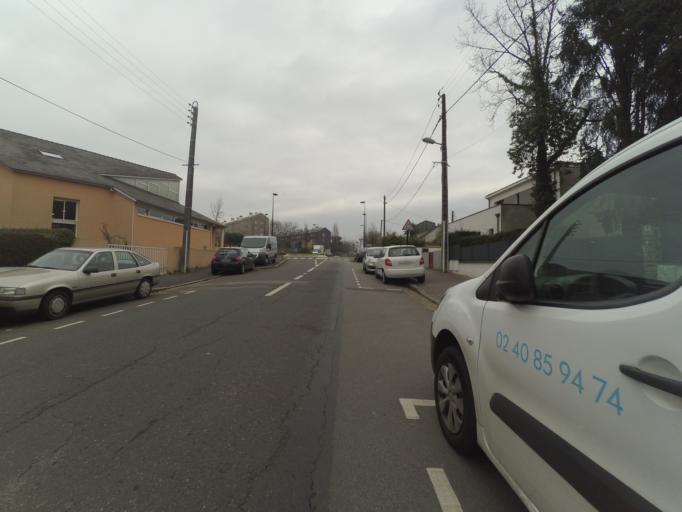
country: FR
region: Pays de la Loire
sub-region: Departement de la Loire-Atlantique
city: Bouguenais
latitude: 47.2177
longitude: -1.6026
